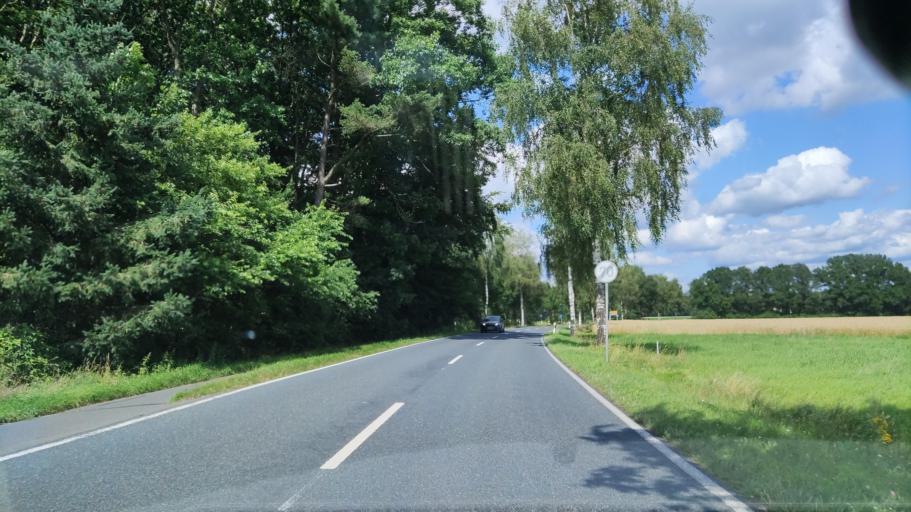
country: DE
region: Lower Saxony
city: Soltau
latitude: 52.9548
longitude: 9.7653
